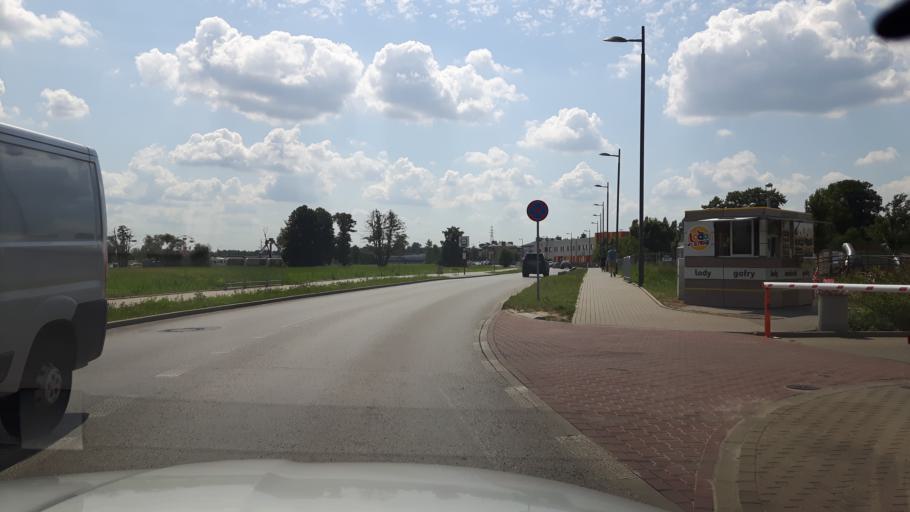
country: PL
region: Masovian Voivodeship
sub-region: Warszawa
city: Targowek
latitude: 52.3136
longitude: 21.0605
